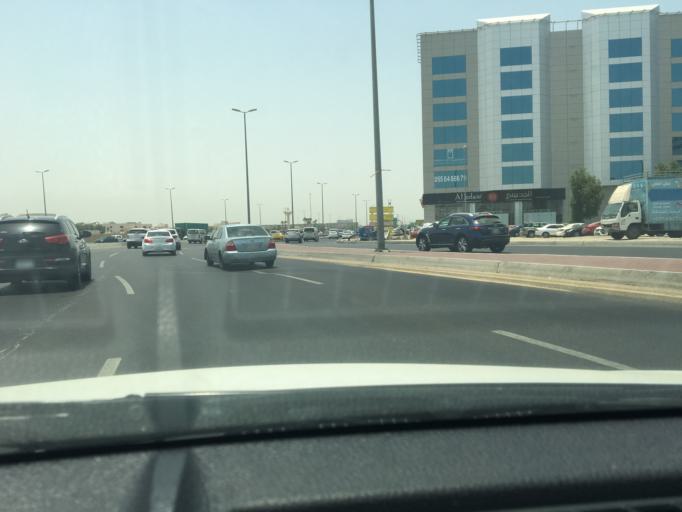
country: SA
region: Makkah
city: Jeddah
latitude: 21.5842
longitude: 39.1767
